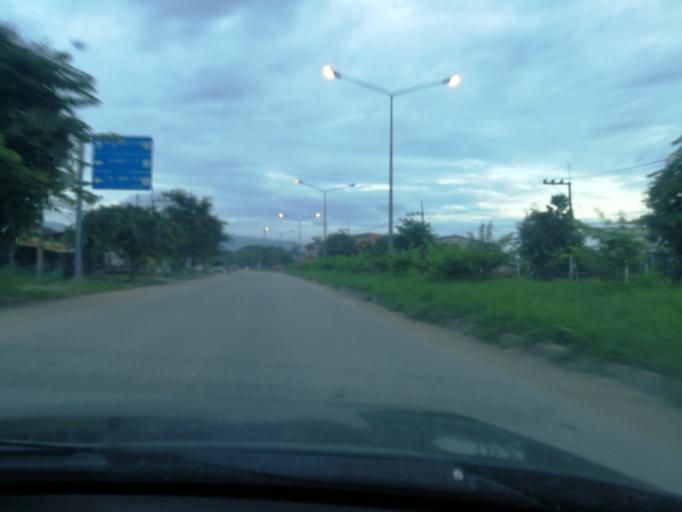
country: TH
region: Chiang Mai
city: Hot
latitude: 18.1865
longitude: 98.6127
